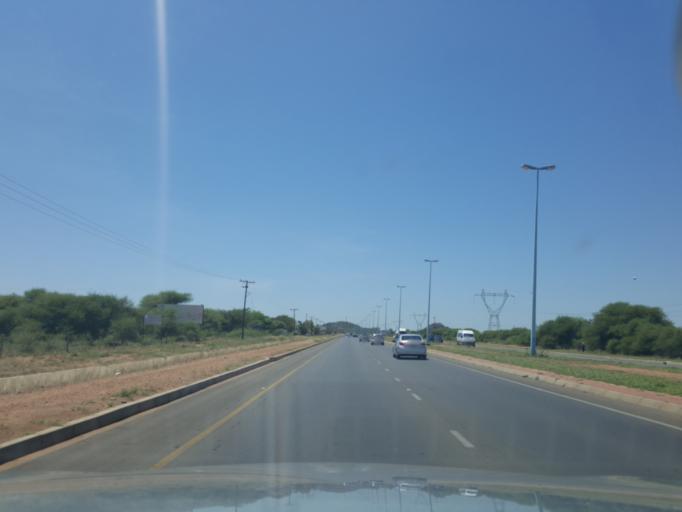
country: BW
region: Kweneng
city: Gaphatshwe
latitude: -24.5835
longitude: 25.8399
